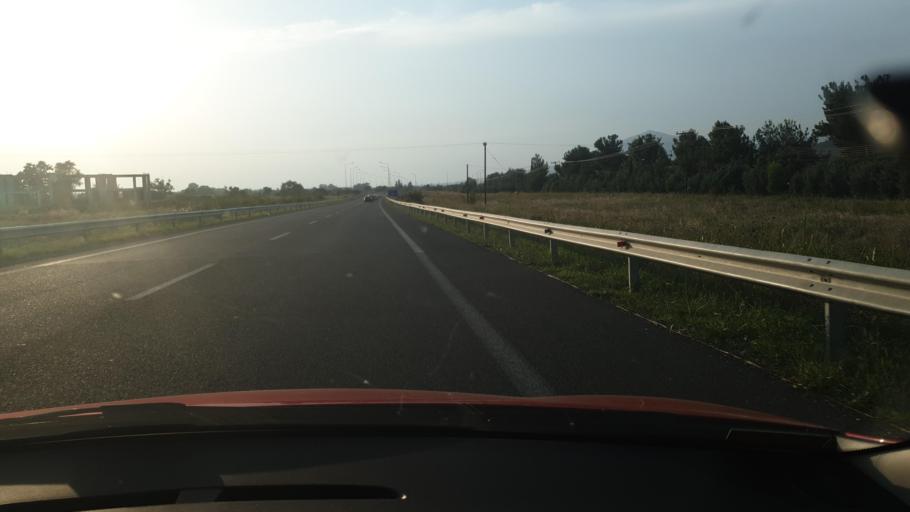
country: GR
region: Central Macedonia
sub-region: Nomos Thessalonikis
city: Vasilika
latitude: 40.4751
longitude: 23.1669
